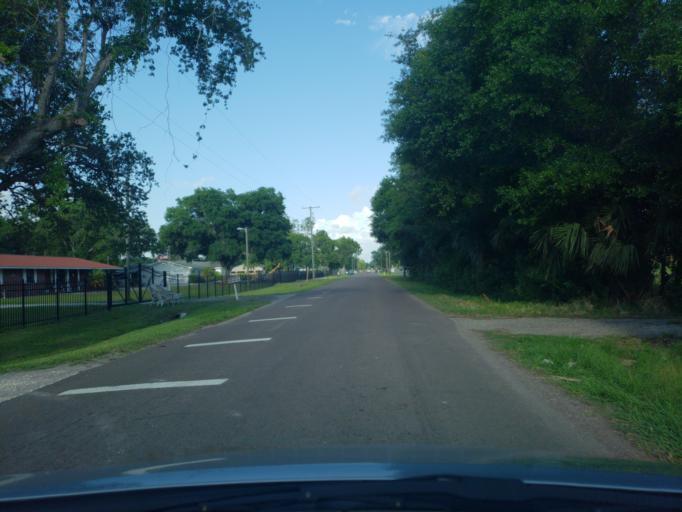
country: US
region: Florida
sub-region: Hillsborough County
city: Palm River-Clair Mel
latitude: 27.9155
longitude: -82.3804
